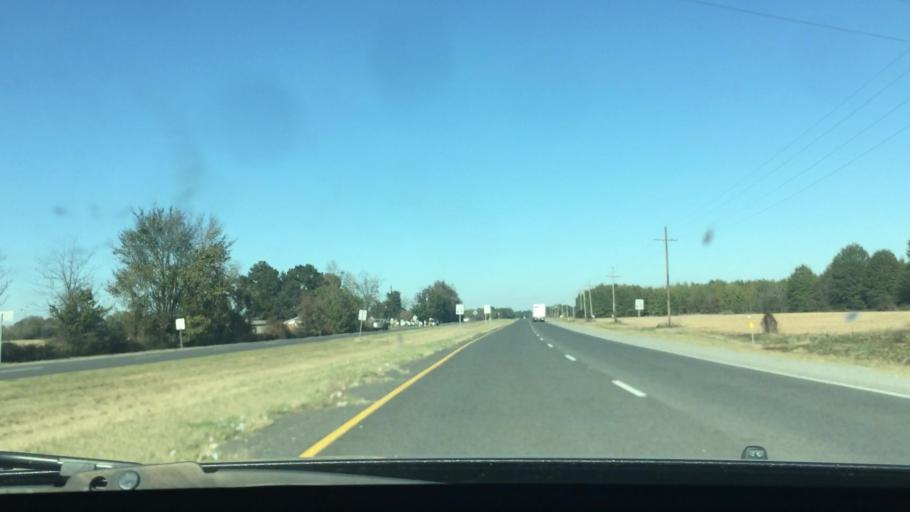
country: US
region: Louisiana
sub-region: Richland Parish
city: Rayville
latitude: 32.3550
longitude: -91.7760
